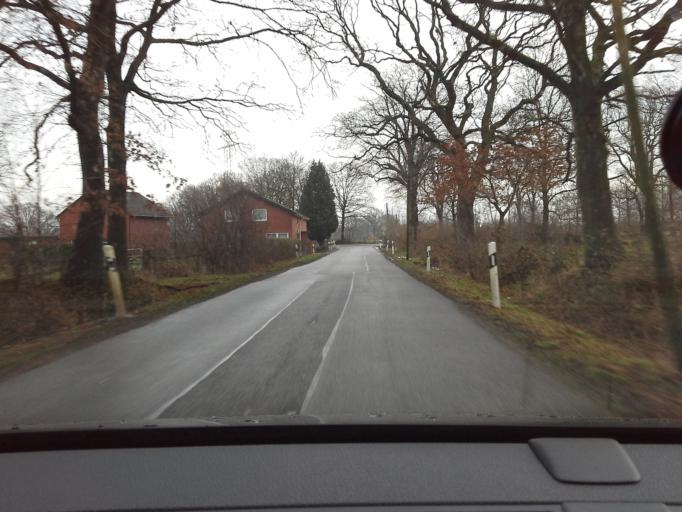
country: DE
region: Schleswig-Holstein
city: Tangstedt
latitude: 53.7445
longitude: 10.0221
